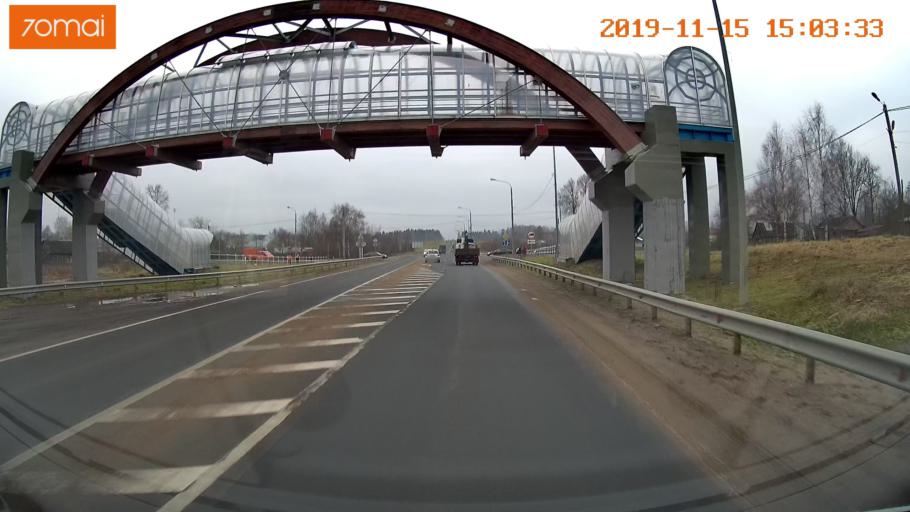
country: RU
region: Jaroslavl
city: Prechistoye
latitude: 58.4235
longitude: 40.3247
